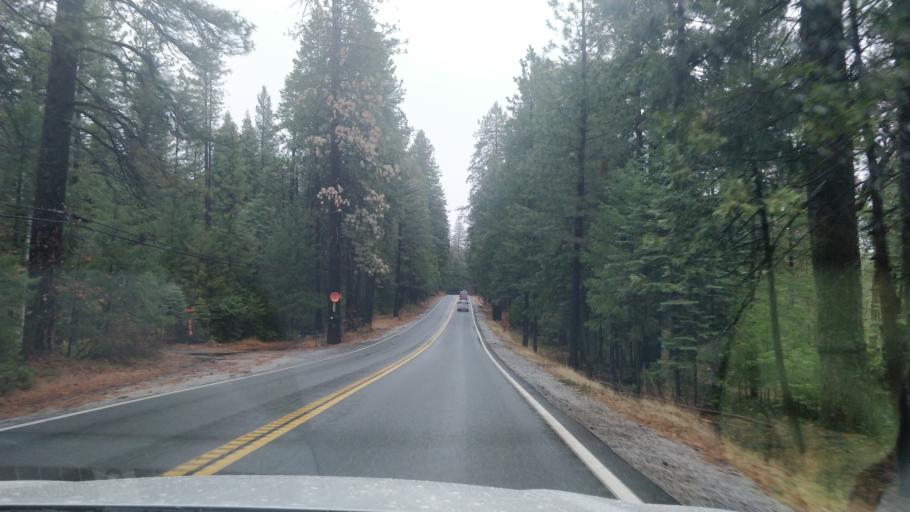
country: US
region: California
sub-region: Nevada County
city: Nevada City
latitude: 39.3203
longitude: -120.8863
